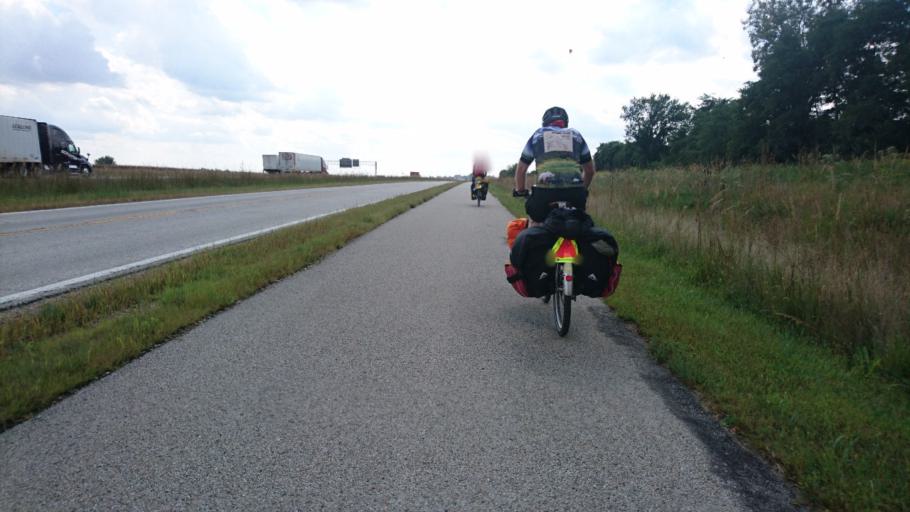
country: US
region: Illinois
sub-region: McLean County
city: Bloomington
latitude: 40.4276
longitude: -89.0377
